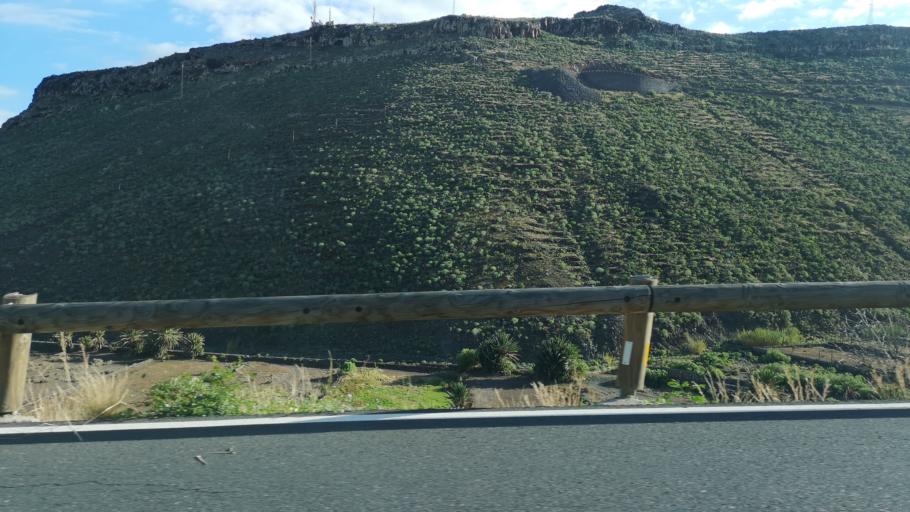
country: ES
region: Canary Islands
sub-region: Provincia de Santa Cruz de Tenerife
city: San Sebastian de la Gomera
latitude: 28.0899
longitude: -17.1214
